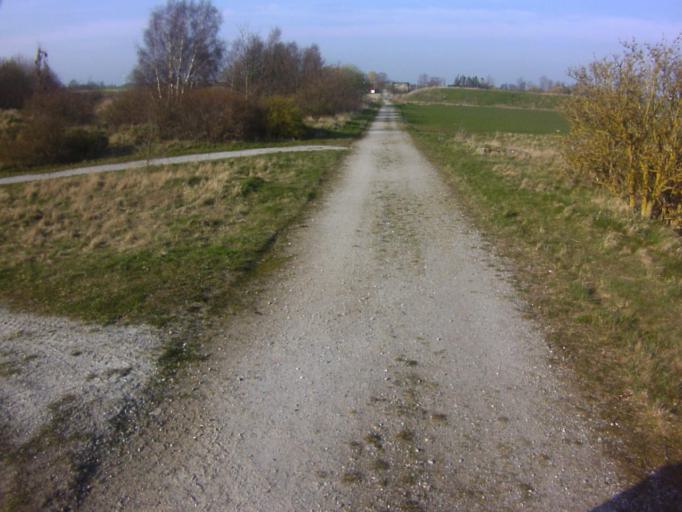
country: SE
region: Skane
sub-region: Kavlinge Kommun
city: Kaevlinge
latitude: 55.7960
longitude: 13.1391
